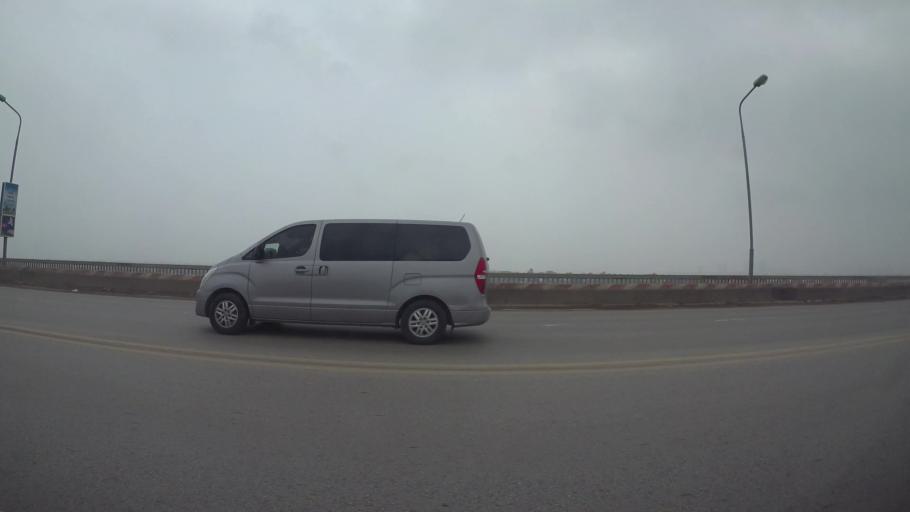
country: VN
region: Ha Noi
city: Tay Ho
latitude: 21.1068
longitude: 105.7871
